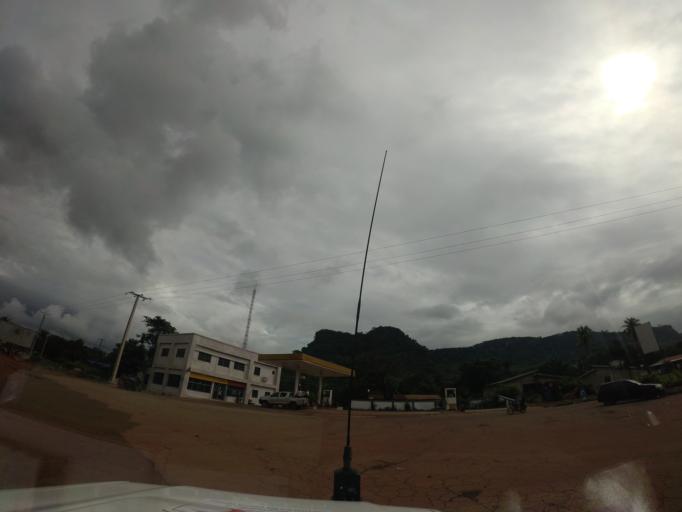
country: GN
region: Kindia
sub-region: Coyah
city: Coyah
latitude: 9.7111
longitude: -13.4003
